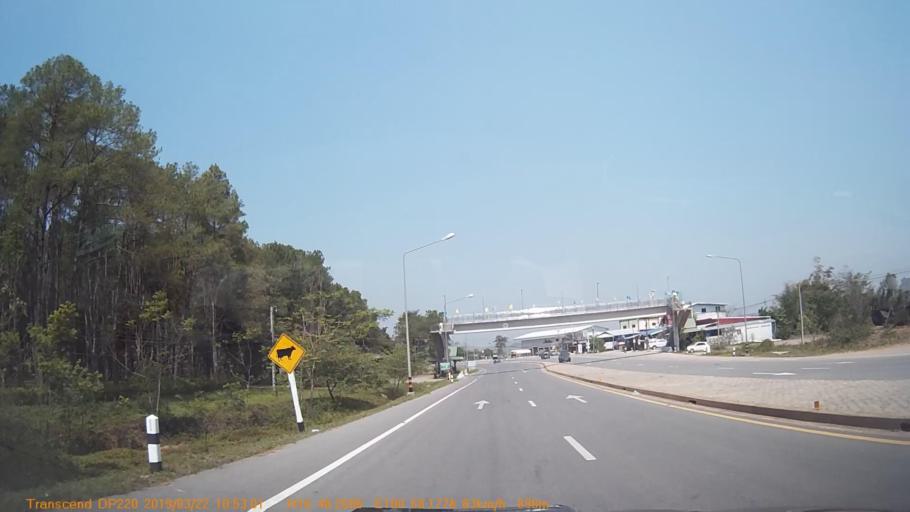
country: TH
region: Phetchabun
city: Khao Kho
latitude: 16.8048
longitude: 100.9692
